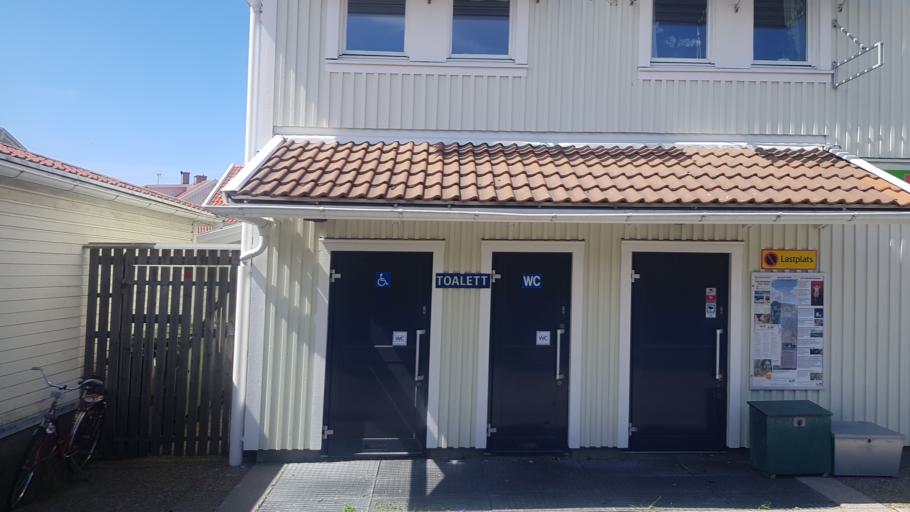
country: SE
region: Vaestra Goetaland
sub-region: Tjorns Kommun
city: Skaerhamn
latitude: 57.9909
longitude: 11.5463
